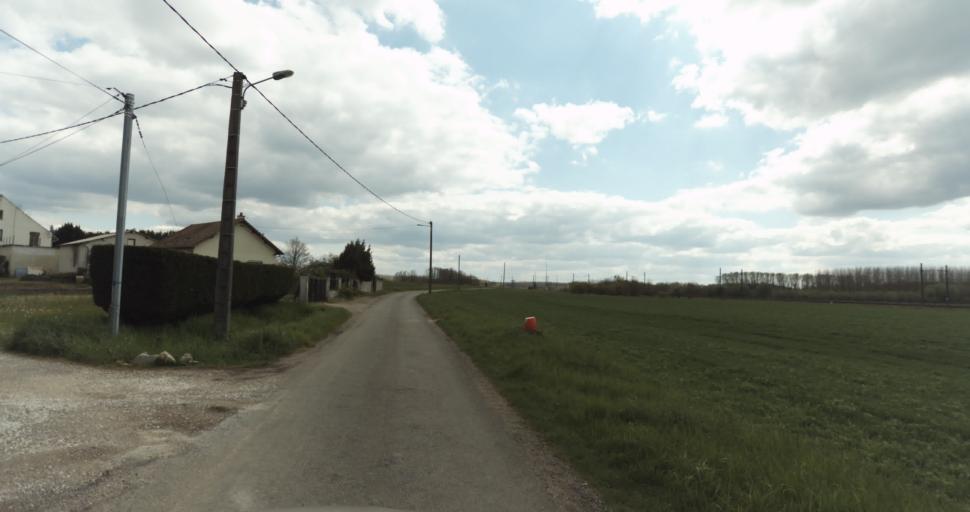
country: FR
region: Bourgogne
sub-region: Departement de la Cote-d'Or
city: Auxonne
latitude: 47.1756
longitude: 5.3946
